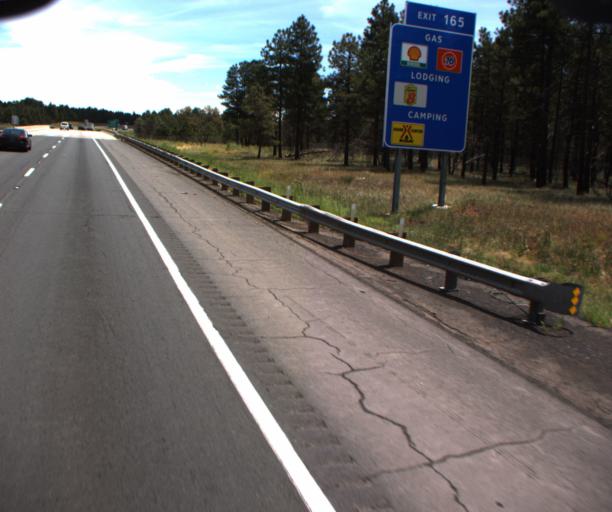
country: US
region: Arizona
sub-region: Coconino County
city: Williams
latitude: 35.2639
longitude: -112.1677
